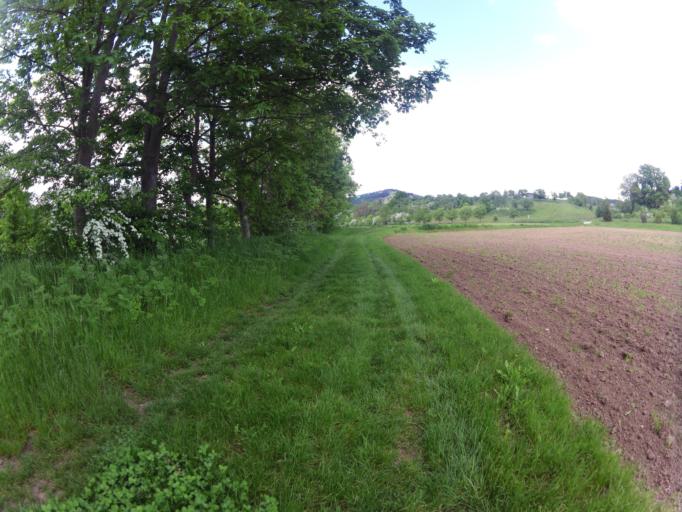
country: DE
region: Thuringia
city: Treffurt
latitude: 51.1179
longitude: 10.2510
